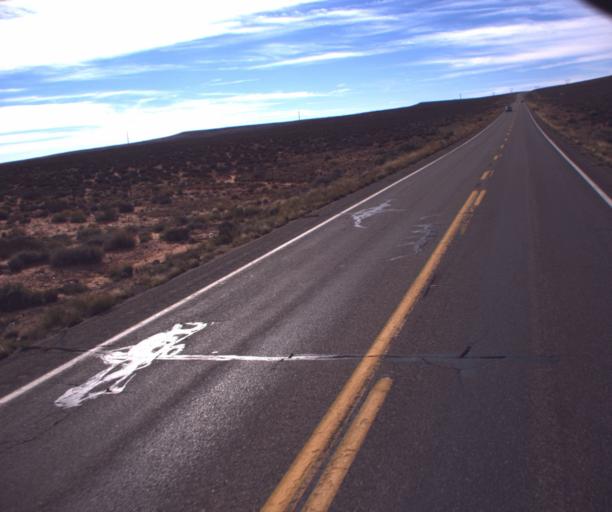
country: US
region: Arizona
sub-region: Coconino County
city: LeChee
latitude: 36.8247
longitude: -111.3090
